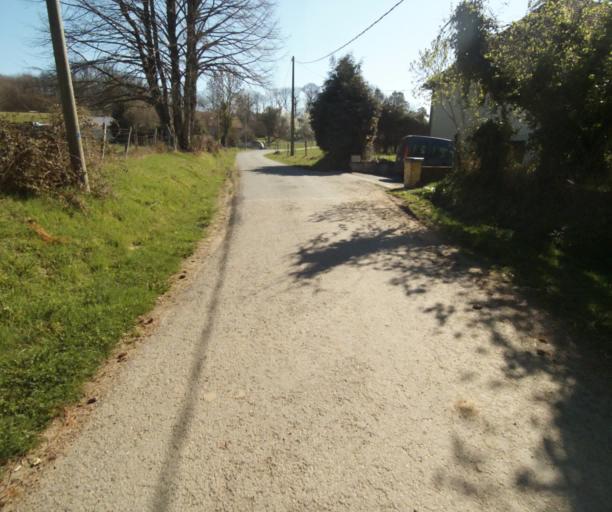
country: FR
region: Limousin
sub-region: Departement de la Correze
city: Saint-Mexant
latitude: 45.3137
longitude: 1.6078
